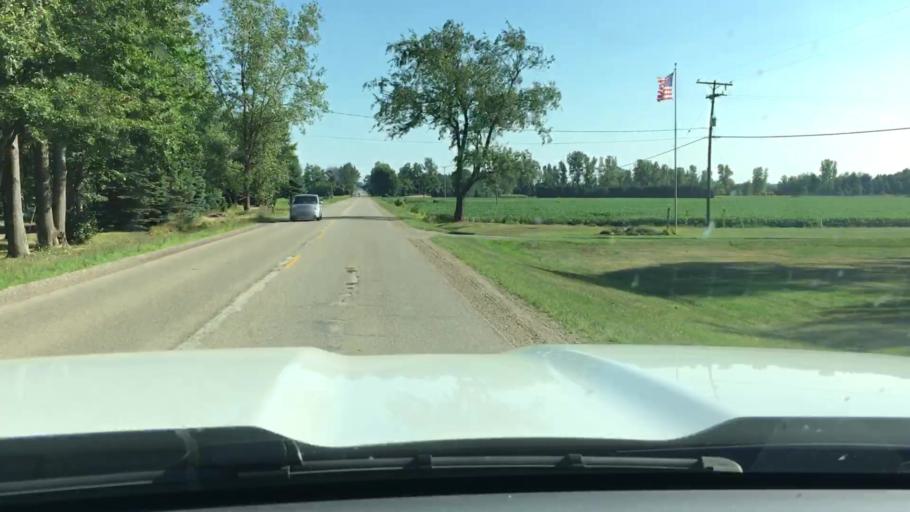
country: US
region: Michigan
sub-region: Ottawa County
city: Zeeland
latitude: 42.8778
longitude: -85.9607
